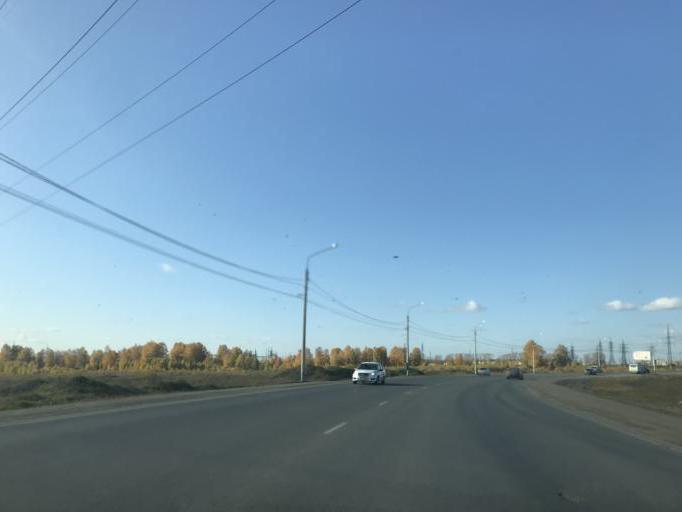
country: RU
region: Chelyabinsk
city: Roshchino
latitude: 55.2257
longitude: 61.2890
